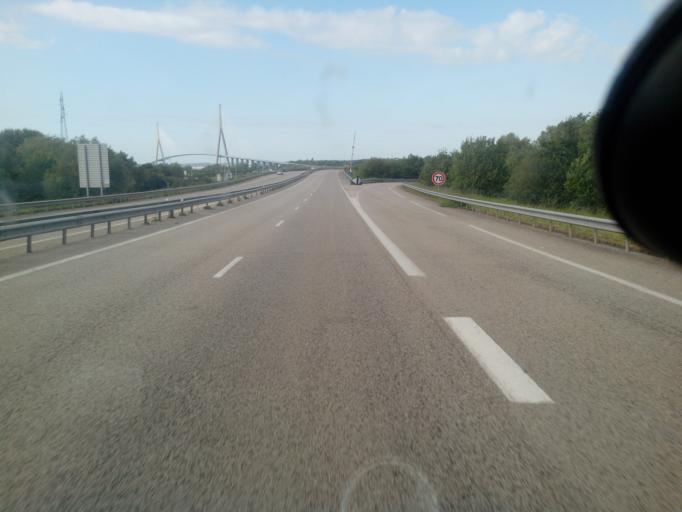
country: FR
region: Lower Normandy
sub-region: Departement du Calvados
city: La Riviere-Saint-Sauveur
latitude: 49.4099
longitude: 0.2681
